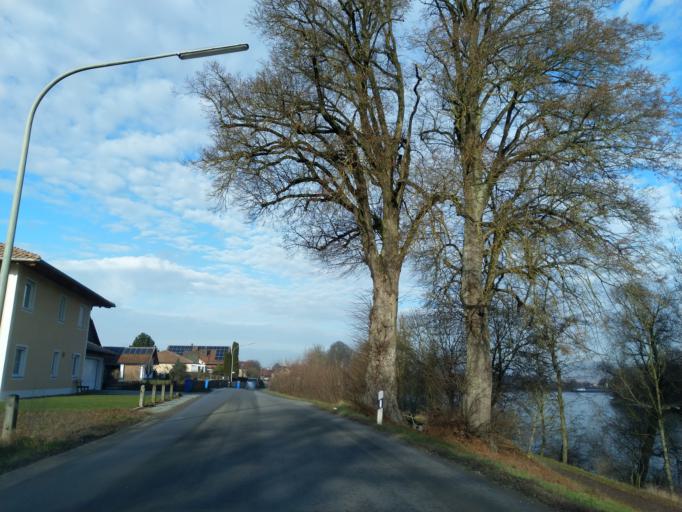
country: DE
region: Bavaria
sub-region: Lower Bavaria
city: Osterhofen
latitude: 48.7200
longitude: 13.0146
